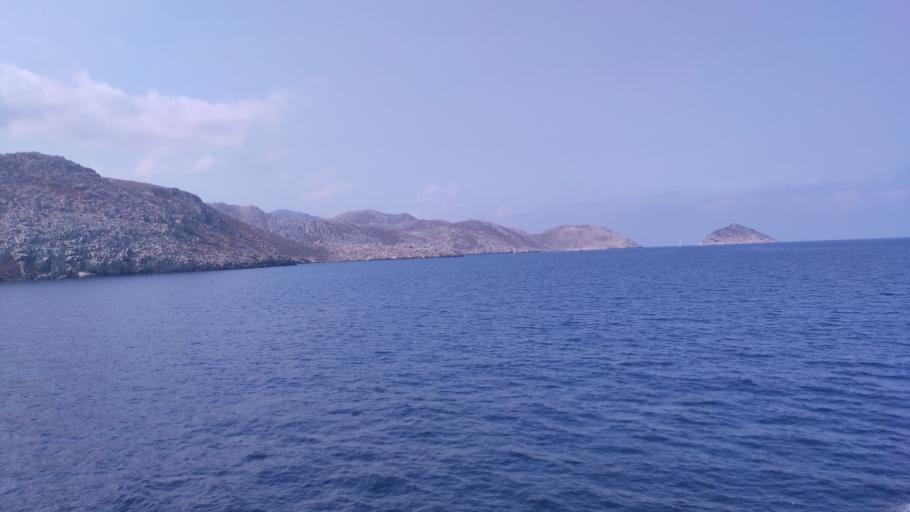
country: GR
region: South Aegean
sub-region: Nomos Dodekanisou
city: Symi
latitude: 36.6443
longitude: 27.8194
